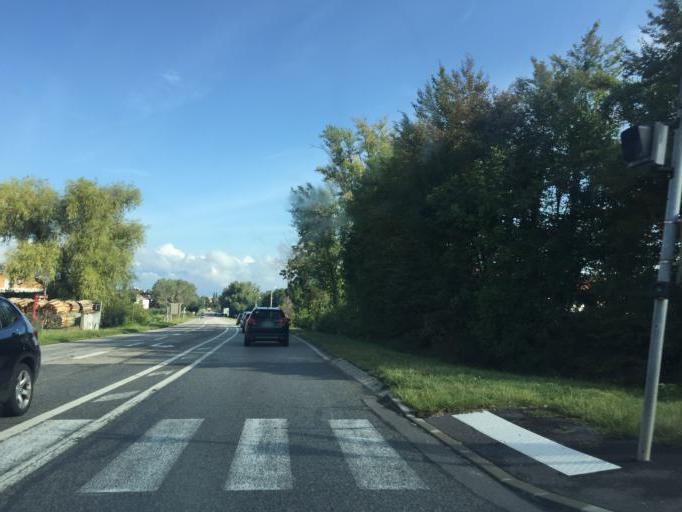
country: FR
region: Rhone-Alpes
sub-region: Departement de la Haute-Savoie
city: Beaumont
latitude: 46.0939
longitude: 6.1040
